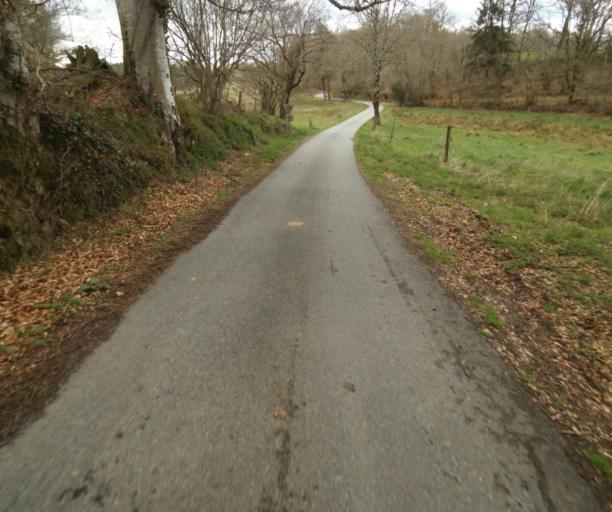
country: FR
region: Limousin
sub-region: Departement de la Correze
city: Correze
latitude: 45.3176
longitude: 1.8896
